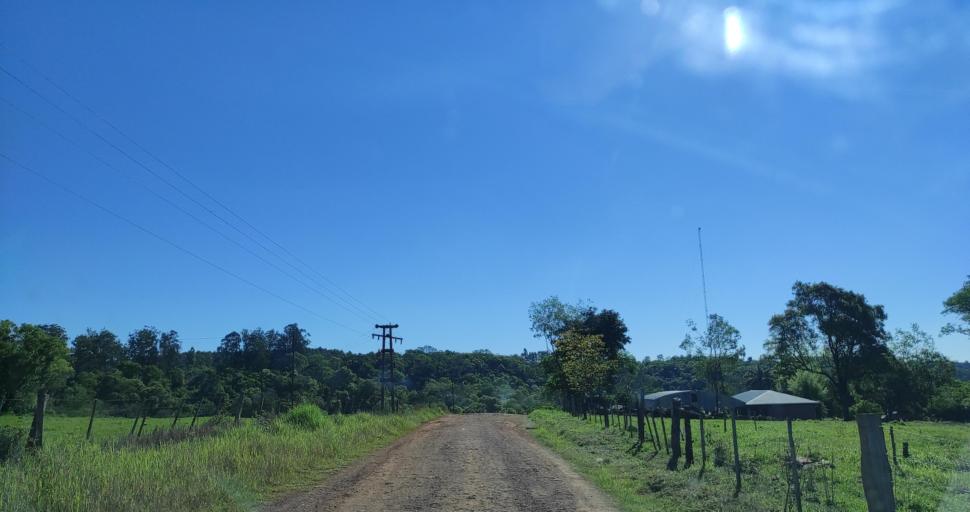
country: AR
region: Misiones
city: Capiovi
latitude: -26.9210
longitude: -55.0767
